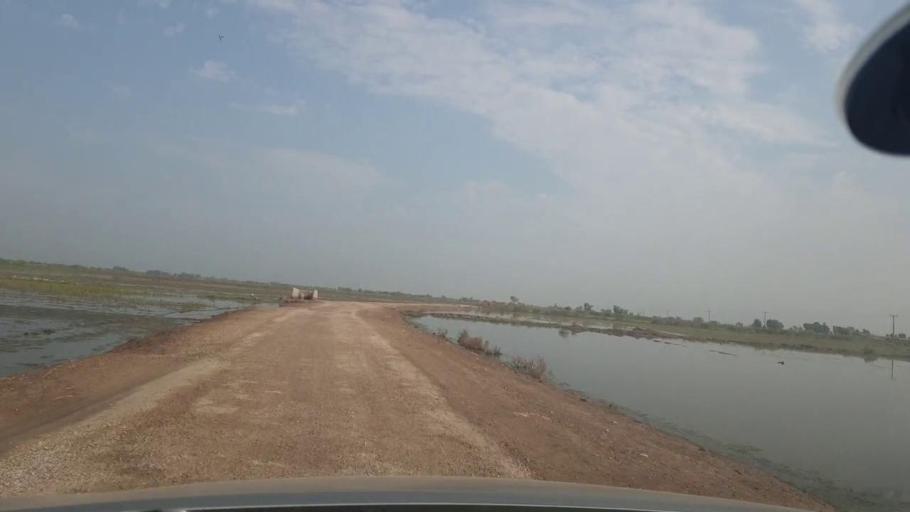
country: PK
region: Balochistan
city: Mehrabpur
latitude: 28.0628
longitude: 68.2101
